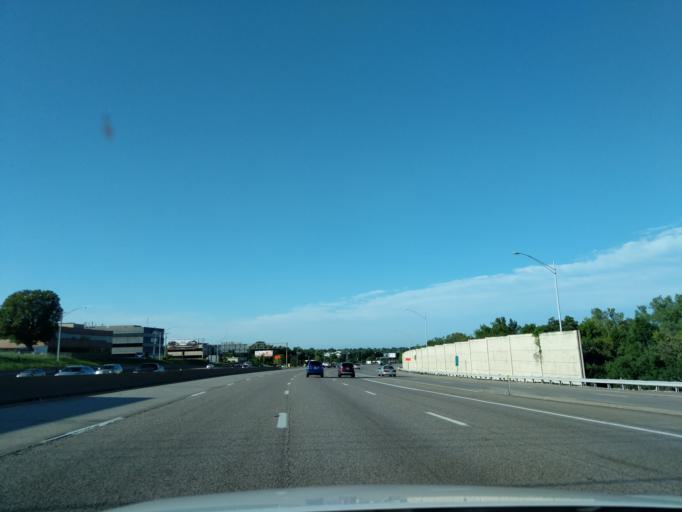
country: US
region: Missouri
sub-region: Saint Louis County
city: Green Park
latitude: 38.5149
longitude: -90.3353
